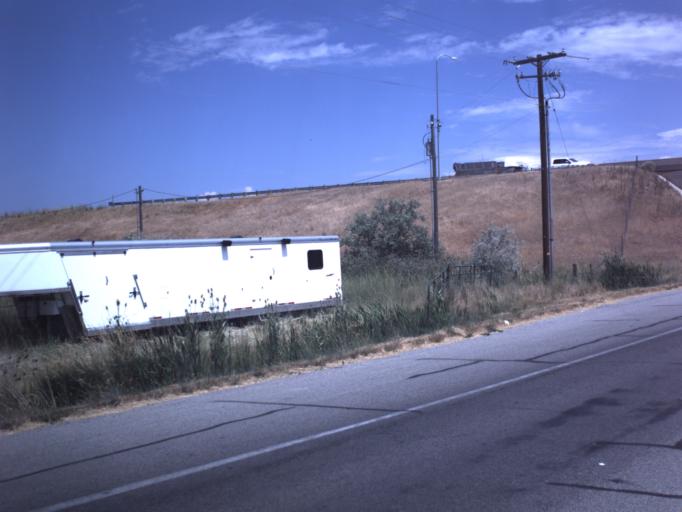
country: US
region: Utah
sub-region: Box Elder County
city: Tremonton
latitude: 41.7111
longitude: -112.1937
